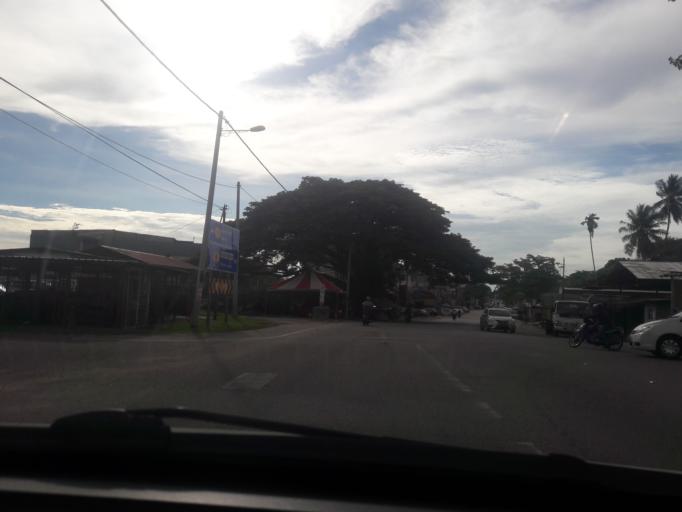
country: MY
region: Kedah
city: Sungai Petani
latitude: 5.6358
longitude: 100.4985
